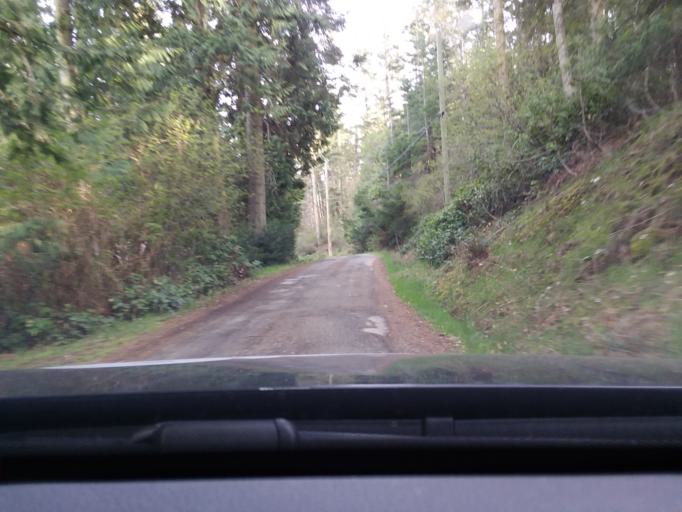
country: CA
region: British Columbia
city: North Saanich
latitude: 48.7409
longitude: -123.2375
